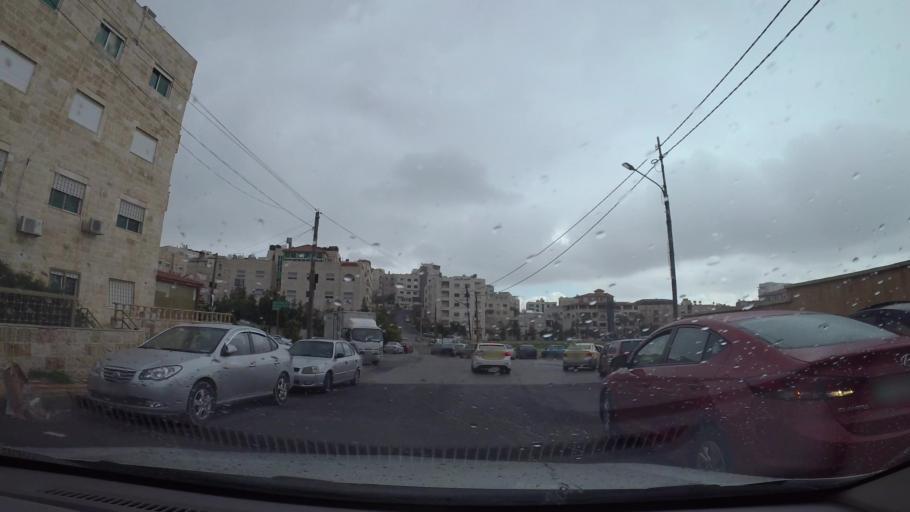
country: JO
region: Amman
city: Al Jubayhah
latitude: 31.9905
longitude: 35.8605
